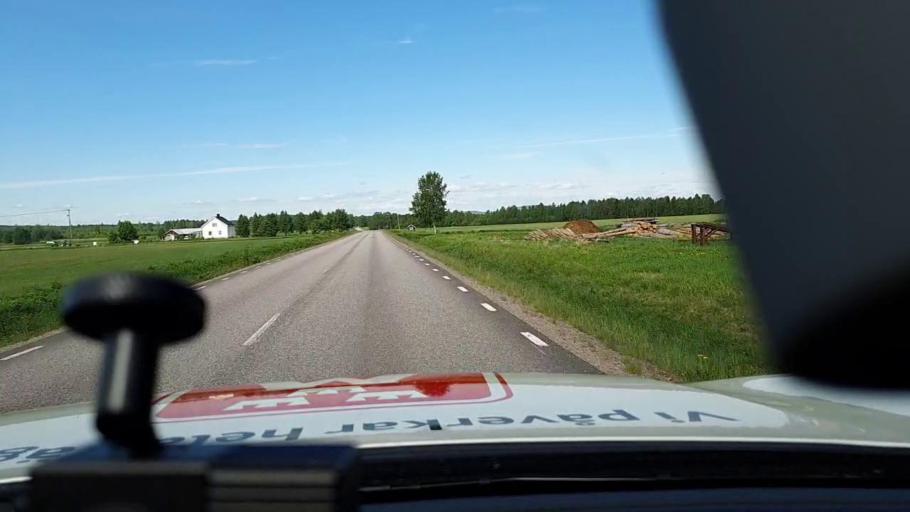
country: SE
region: Norrbotten
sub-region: Lulea Kommun
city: Sodra Sunderbyn
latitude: 65.6498
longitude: 21.8728
